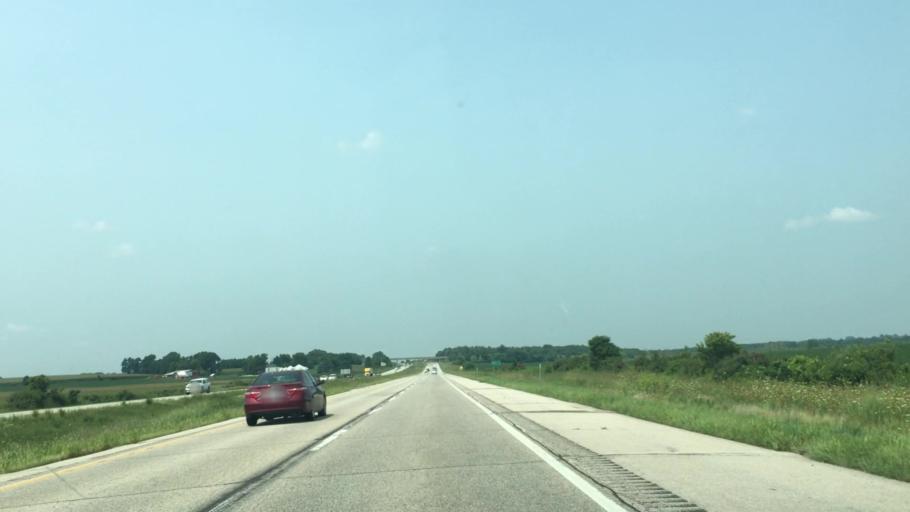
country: US
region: Iowa
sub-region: Linn County
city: Center Point
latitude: 42.1785
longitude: -91.7904
